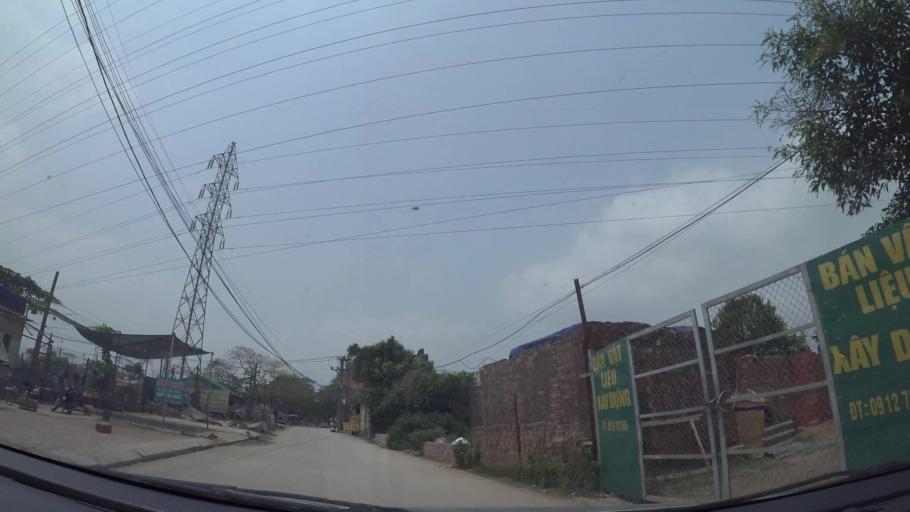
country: VN
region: Ha Noi
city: Tay Ho
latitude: 21.0847
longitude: 105.8105
